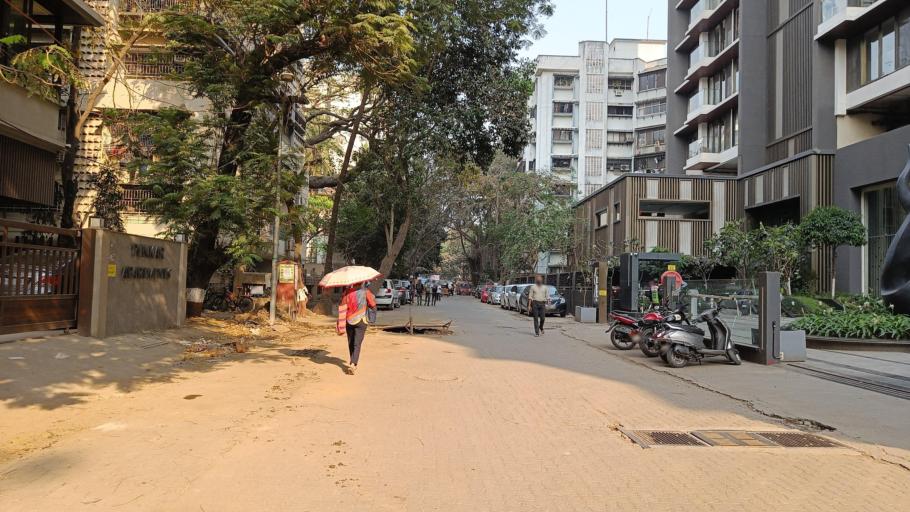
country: IN
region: Maharashtra
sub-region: Mumbai Suburban
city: Mumbai
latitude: 19.0820
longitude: 72.8365
